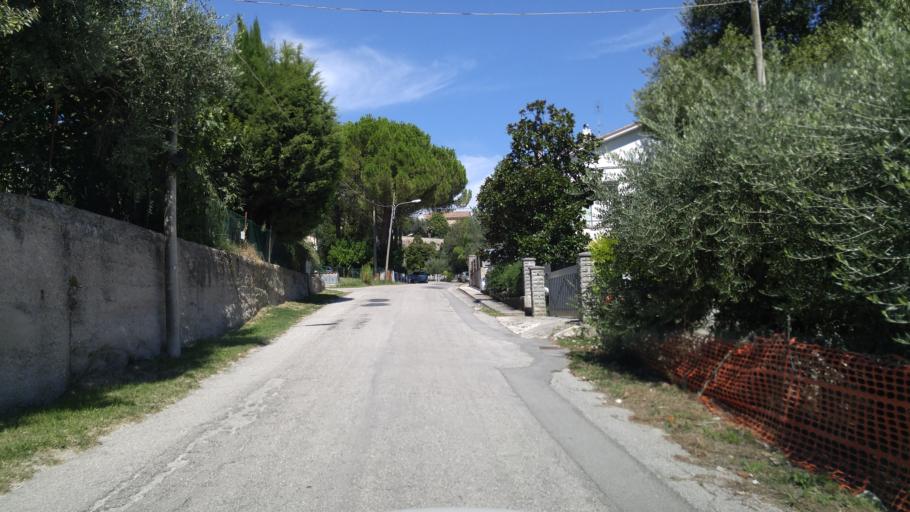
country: IT
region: The Marches
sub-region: Provincia di Pesaro e Urbino
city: San Giorgio di Pesaro
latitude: 43.7148
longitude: 12.9722
